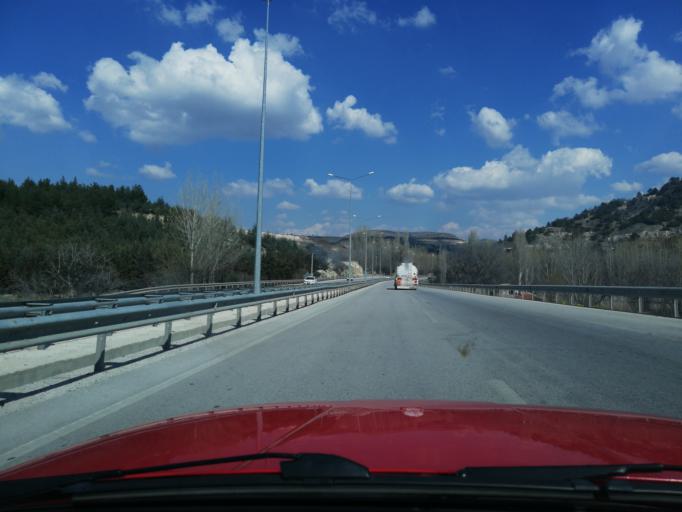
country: TR
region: Burdur
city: Burdur
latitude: 37.6979
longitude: 30.3312
